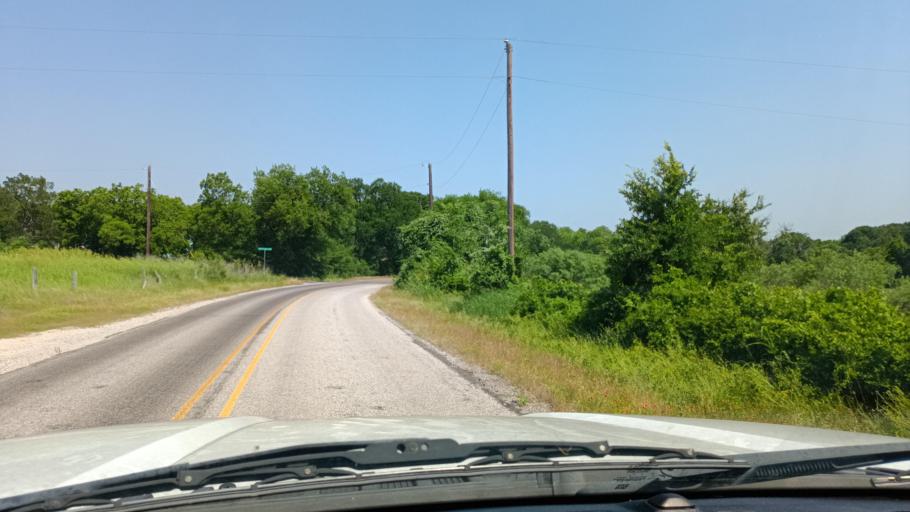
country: US
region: Texas
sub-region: Bell County
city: Morgans Point Resort
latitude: 31.1205
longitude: -97.5370
